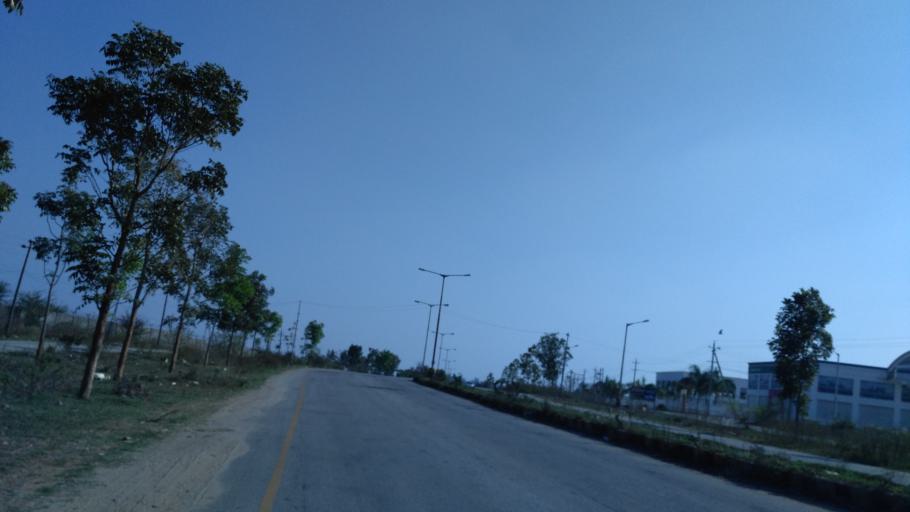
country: IN
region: Karnataka
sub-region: Hassan
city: Hassan
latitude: 12.9674
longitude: 76.1235
